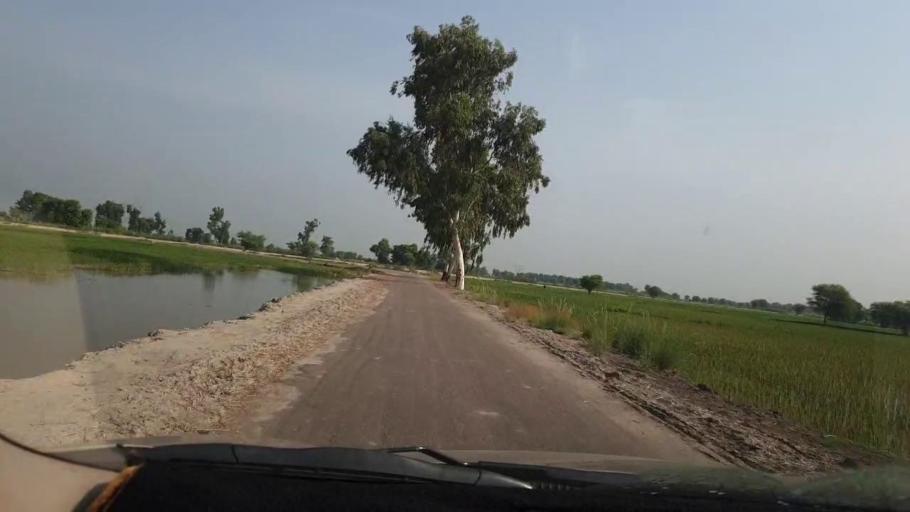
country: PK
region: Sindh
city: Goth Garelo
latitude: 27.4711
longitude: 68.0787
